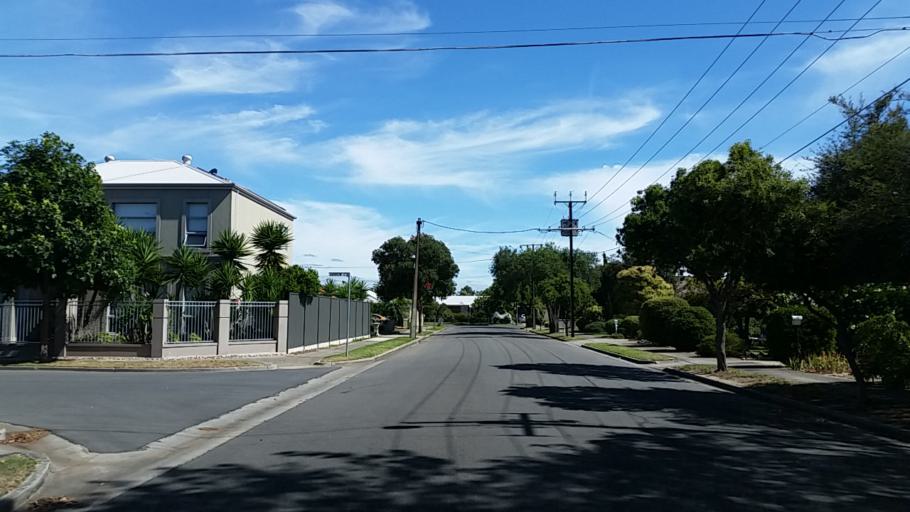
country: AU
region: South Australia
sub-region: Charles Sturt
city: Findon
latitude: -34.9202
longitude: 138.5252
